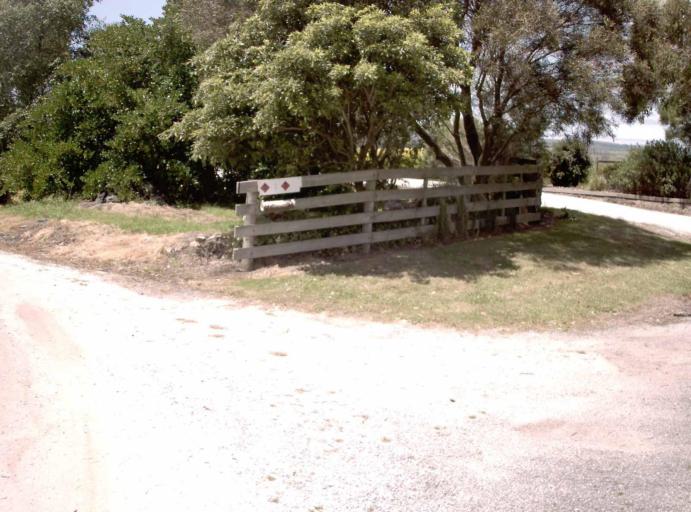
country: AU
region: Victoria
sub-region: Bass Coast
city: North Wonthaggi
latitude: -38.5882
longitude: 146.0216
